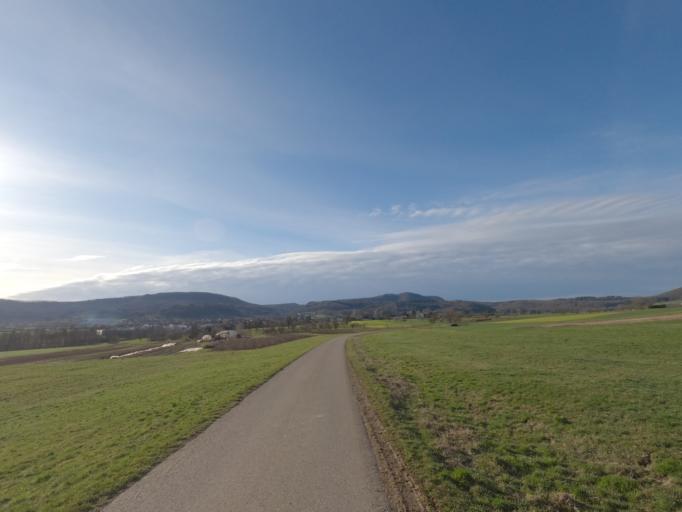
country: DE
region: Baden-Wuerttemberg
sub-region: Regierungsbezirk Stuttgart
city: Boll
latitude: 48.6534
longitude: 9.6087
